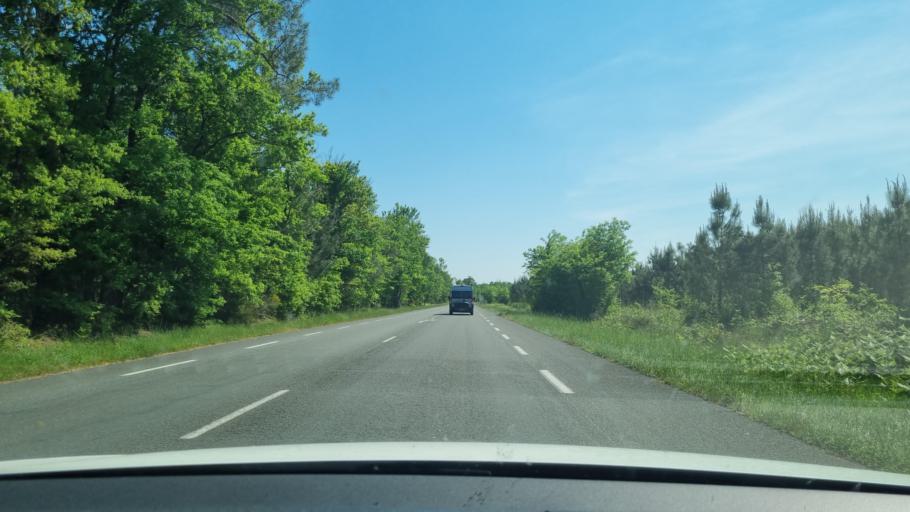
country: FR
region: Aquitaine
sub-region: Departement de la Gironde
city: Prechac
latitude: 44.2356
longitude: -0.2608
